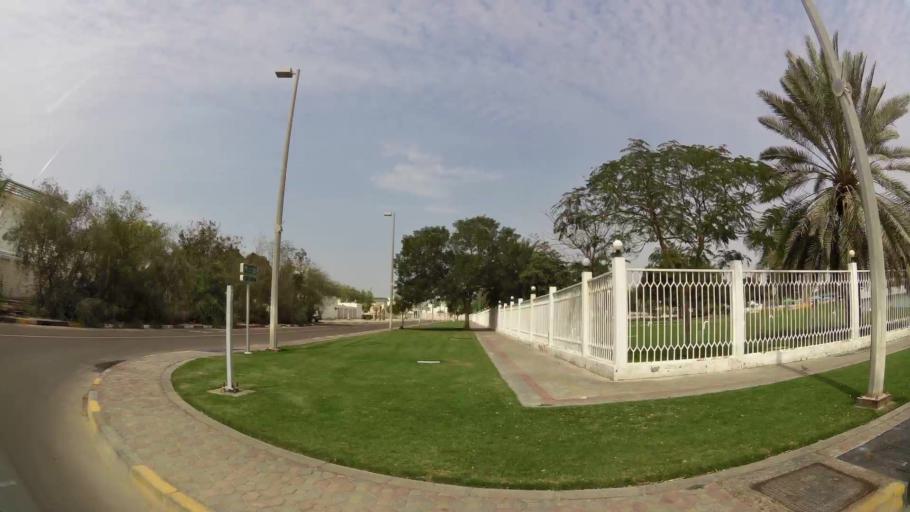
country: AE
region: Abu Dhabi
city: Abu Dhabi
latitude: 24.5359
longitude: 54.6900
